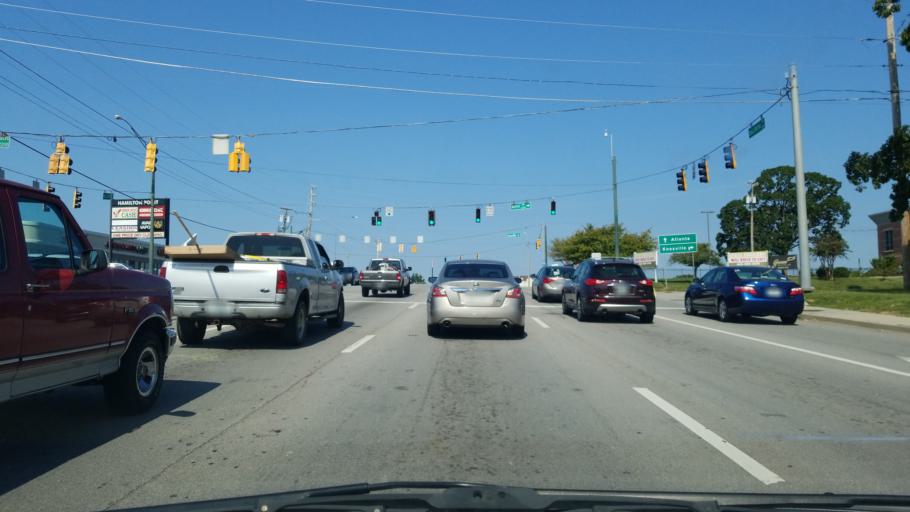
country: US
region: Tennessee
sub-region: Hamilton County
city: East Brainerd
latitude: 35.0417
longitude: -85.1536
